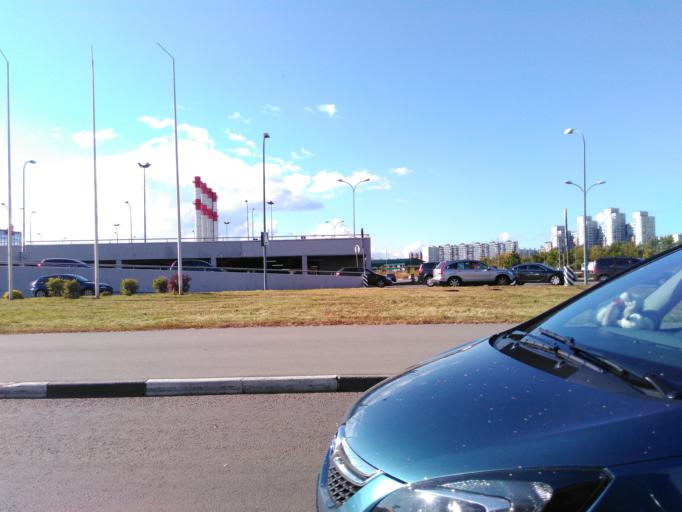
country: RU
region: Moscow
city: Otradnoye
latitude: 55.8513
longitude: 37.6005
